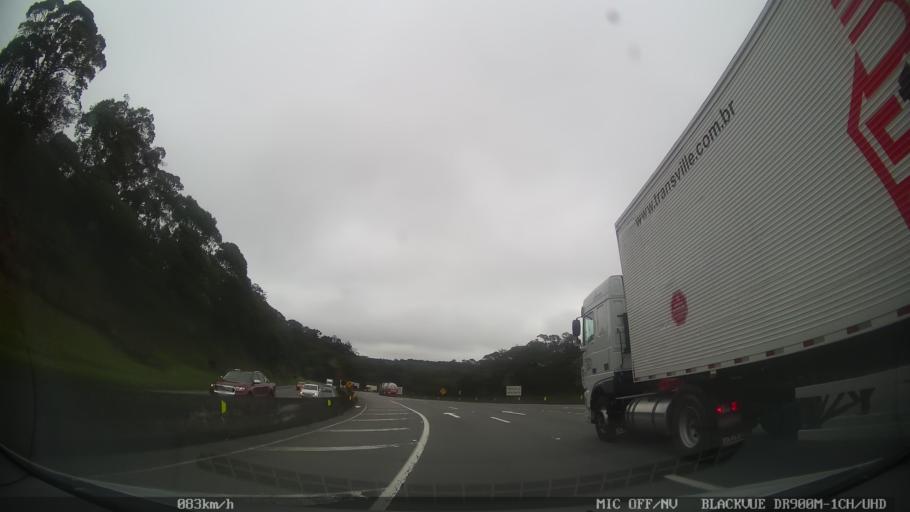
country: BR
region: Parana
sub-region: Sao Jose Dos Pinhais
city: Sao Jose dos Pinhais
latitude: -25.8461
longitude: -49.0664
